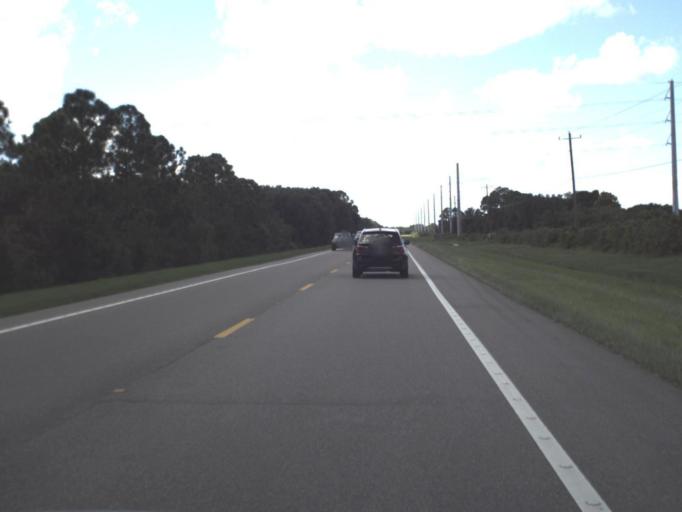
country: US
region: Florida
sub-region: Sarasota County
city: The Meadows
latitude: 27.4154
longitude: -82.3519
